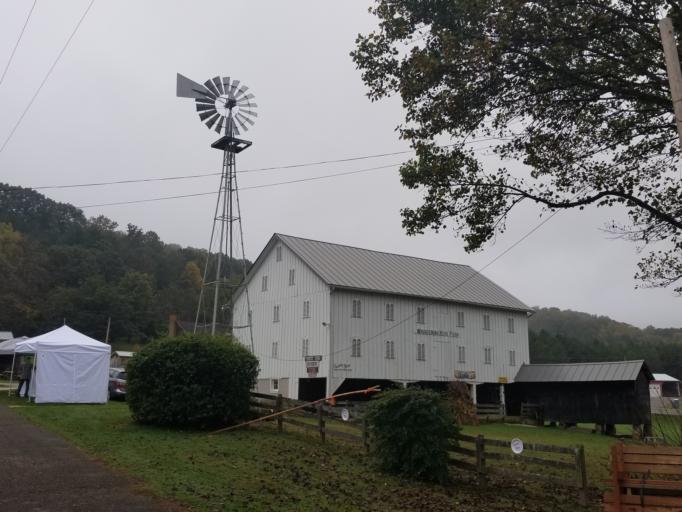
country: US
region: Ohio
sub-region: Carroll County
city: Carrollton
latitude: 40.5126
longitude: -81.1118
